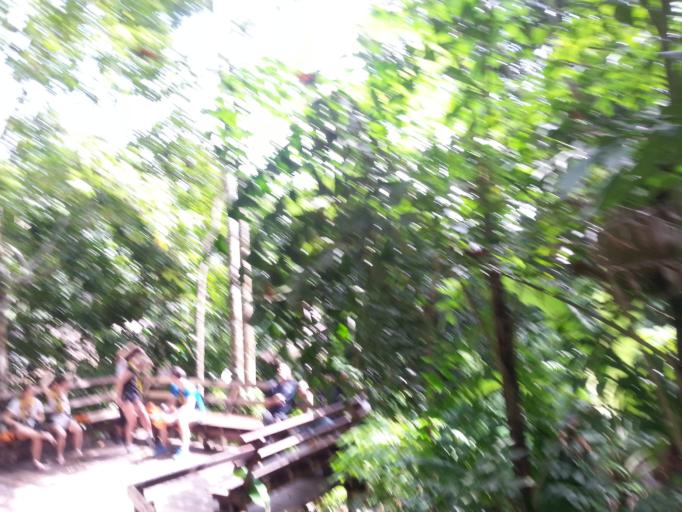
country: TH
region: Phuket
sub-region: Amphoe Kathu
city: Kathu
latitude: 7.9246
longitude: 98.3224
